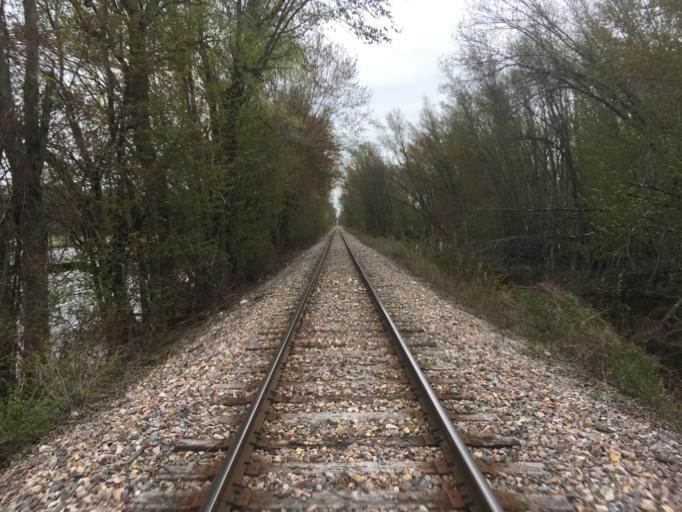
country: US
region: Vermont
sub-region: Addison County
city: Middlebury (village)
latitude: 43.9489
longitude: -73.1619
